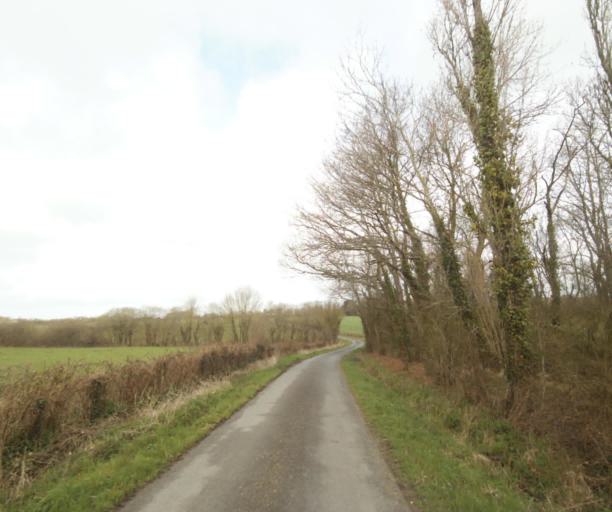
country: FR
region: Pays de la Loire
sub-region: Departement de la Loire-Atlantique
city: Bouvron
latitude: 47.4068
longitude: -1.8689
